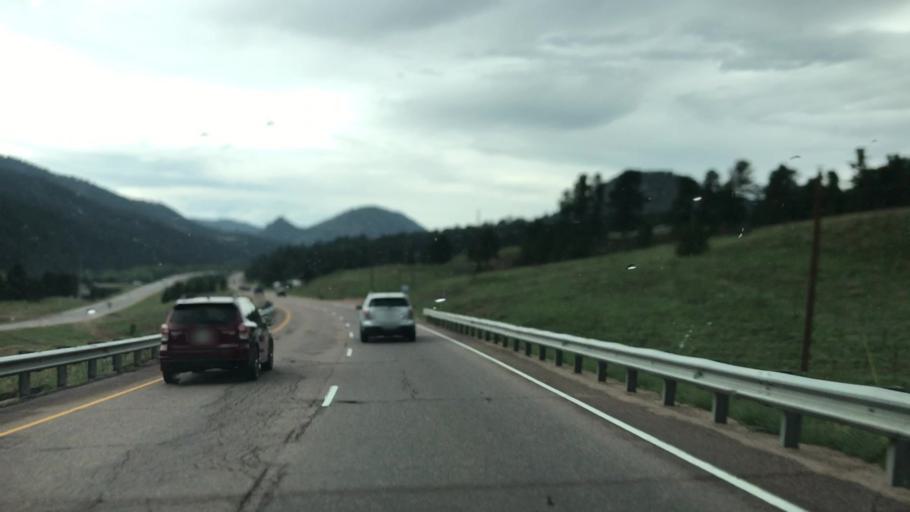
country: US
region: Colorado
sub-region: El Paso County
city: Cascade-Chipita Park
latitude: 38.9386
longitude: -105.0107
